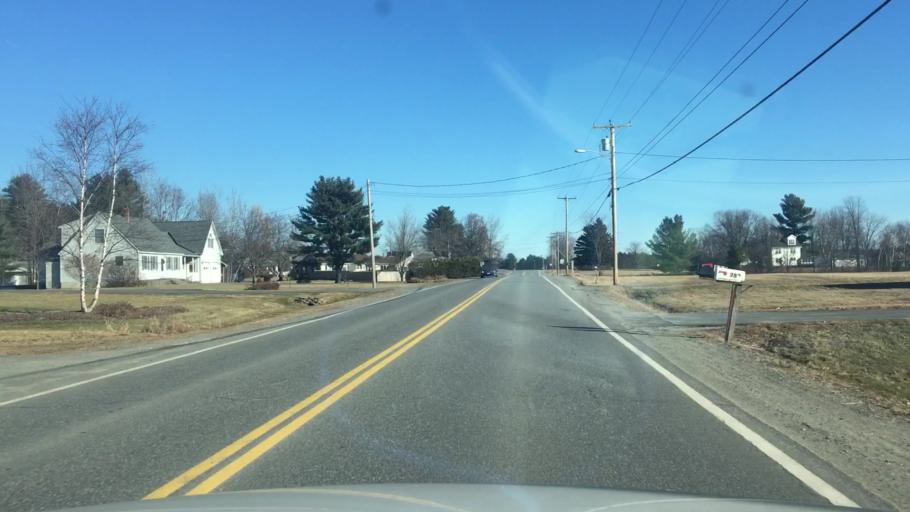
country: US
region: Maine
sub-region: Kennebec County
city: Winslow
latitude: 44.5466
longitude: -69.5981
